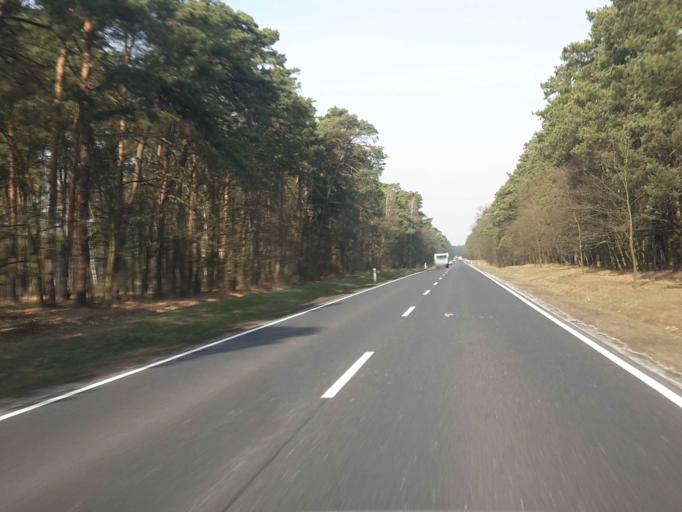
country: PL
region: Kujawsko-Pomorskie
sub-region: Powiat torunski
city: Wielka Nieszawka
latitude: 53.0192
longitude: 18.4274
